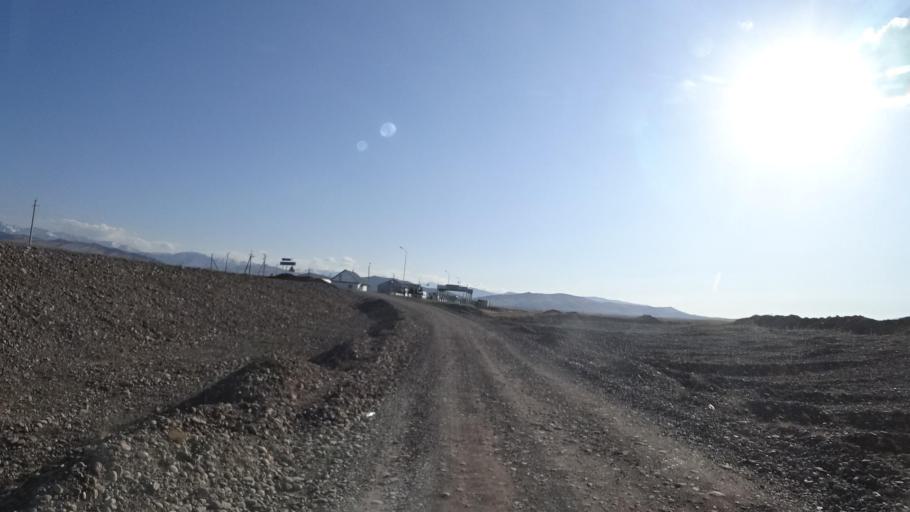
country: KZ
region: Almaty Oblysy
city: Kegen
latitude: 42.8033
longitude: 79.1835
